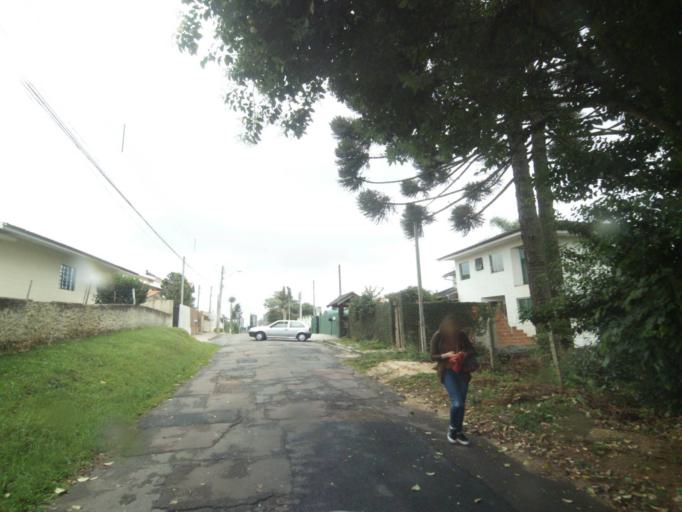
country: BR
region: Parana
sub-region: Curitiba
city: Curitiba
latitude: -25.4224
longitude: -49.3239
